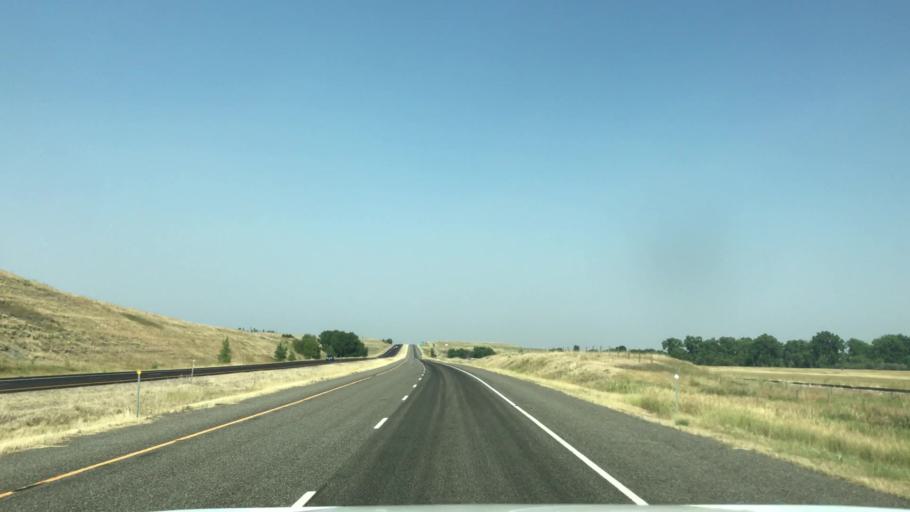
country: US
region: Montana
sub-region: Cascade County
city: Sun Prairie
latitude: 47.2401
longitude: -111.7320
